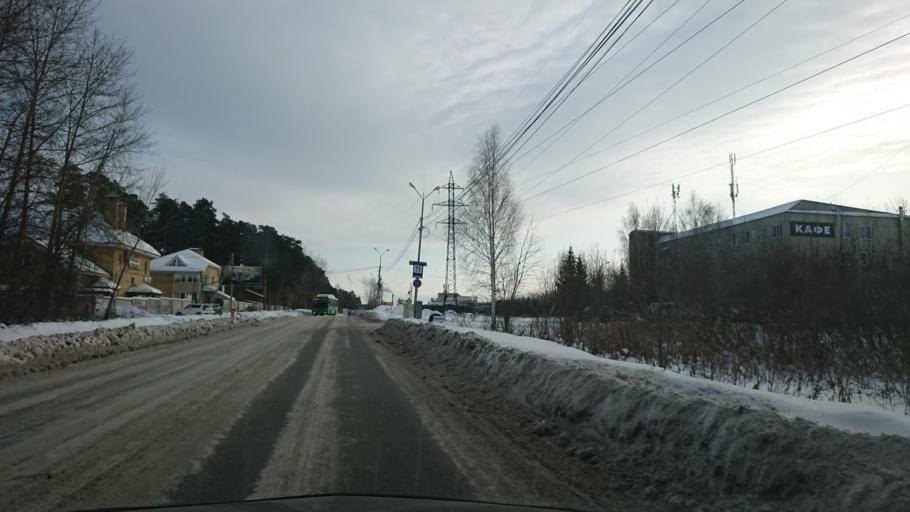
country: RU
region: Sverdlovsk
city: Sovkhoznyy
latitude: 56.7792
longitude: 60.5619
